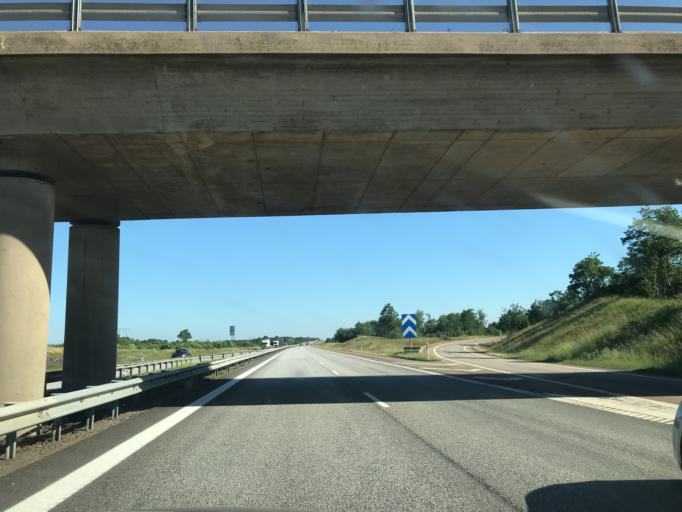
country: SE
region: Halland
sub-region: Varbergs Kommun
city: Tvaaker
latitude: 57.0627
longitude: 12.3566
